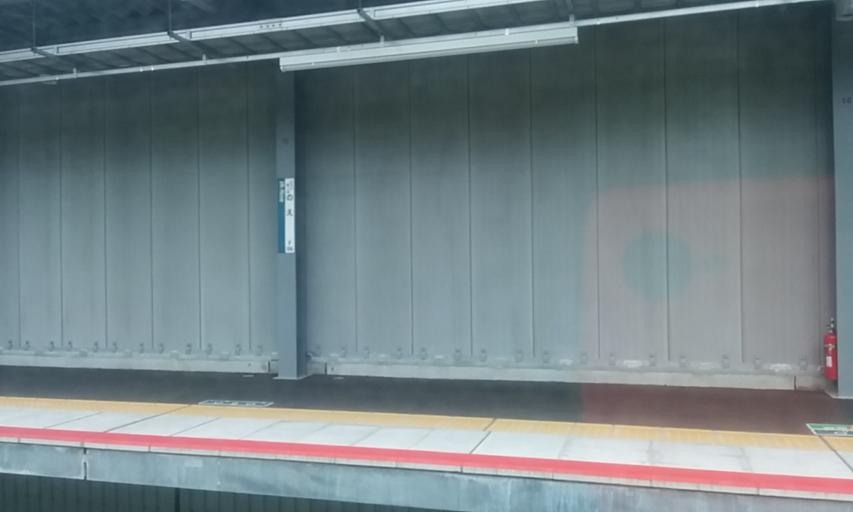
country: JP
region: Osaka
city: Moriguchi
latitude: 34.7065
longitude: 135.5413
